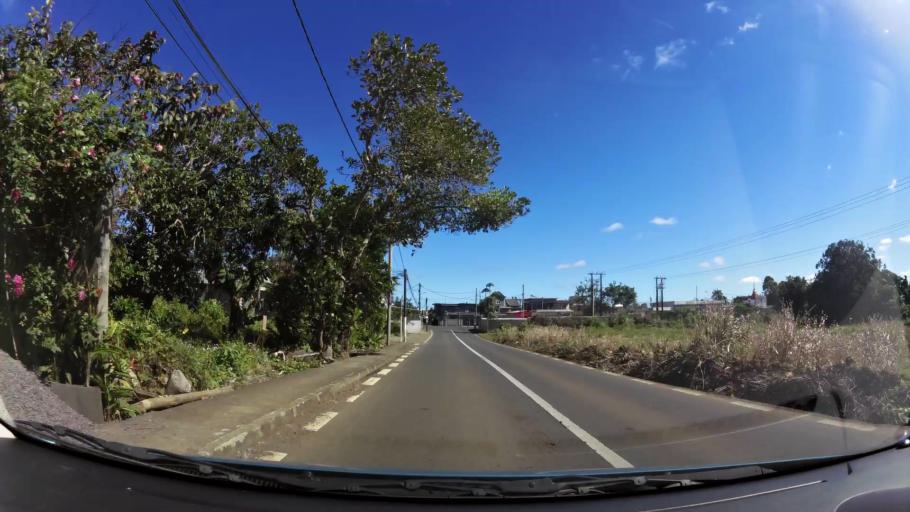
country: MU
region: Plaines Wilhems
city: Curepipe
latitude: -20.3406
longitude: 57.4933
